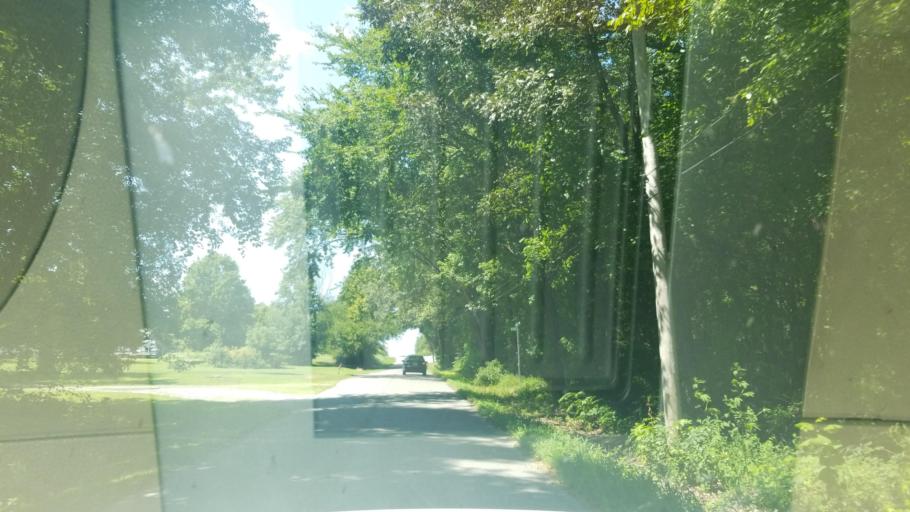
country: US
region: Illinois
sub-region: Saline County
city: Carrier Mills
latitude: 37.7941
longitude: -88.6455
